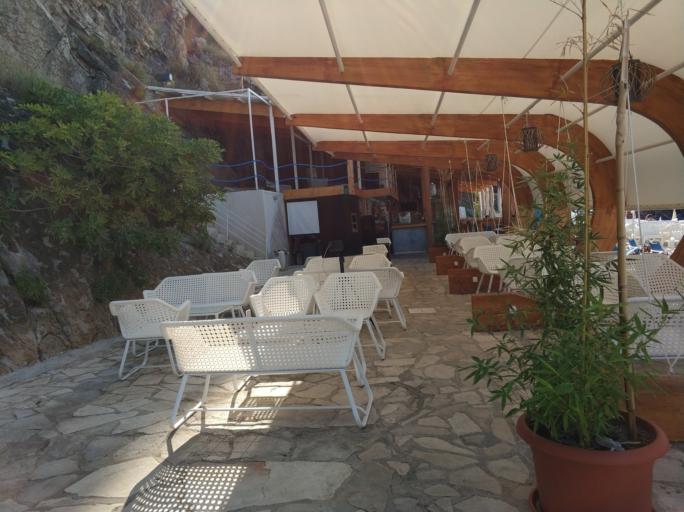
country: ME
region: Budva
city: Budva
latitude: 42.2774
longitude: 18.8809
